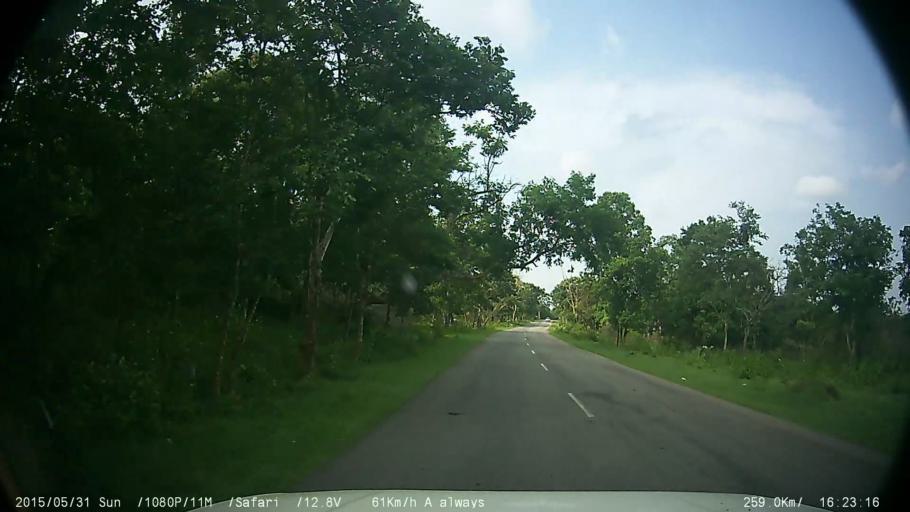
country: IN
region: Karnataka
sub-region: Chamrajnagar
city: Gundlupet
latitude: 11.7576
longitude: 76.5152
